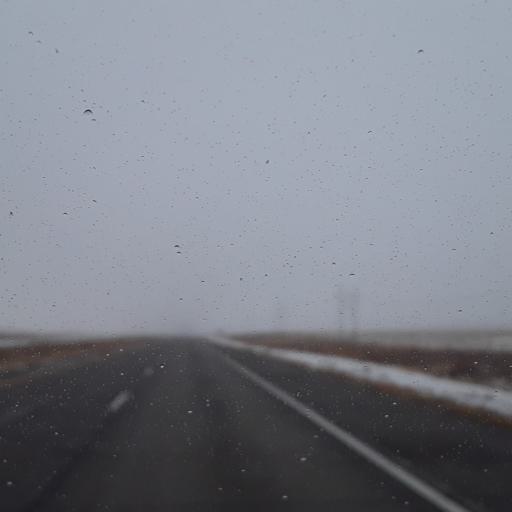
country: US
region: Colorado
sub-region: Logan County
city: Sterling
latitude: 40.7737
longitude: -102.9308
